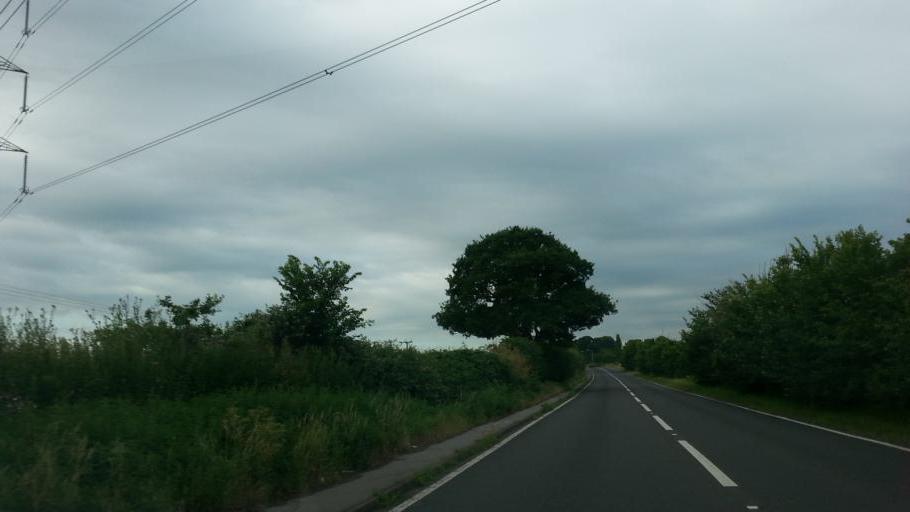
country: GB
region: England
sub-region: Nottinghamshire
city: Farndon
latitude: 53.0473
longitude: -0.8673
